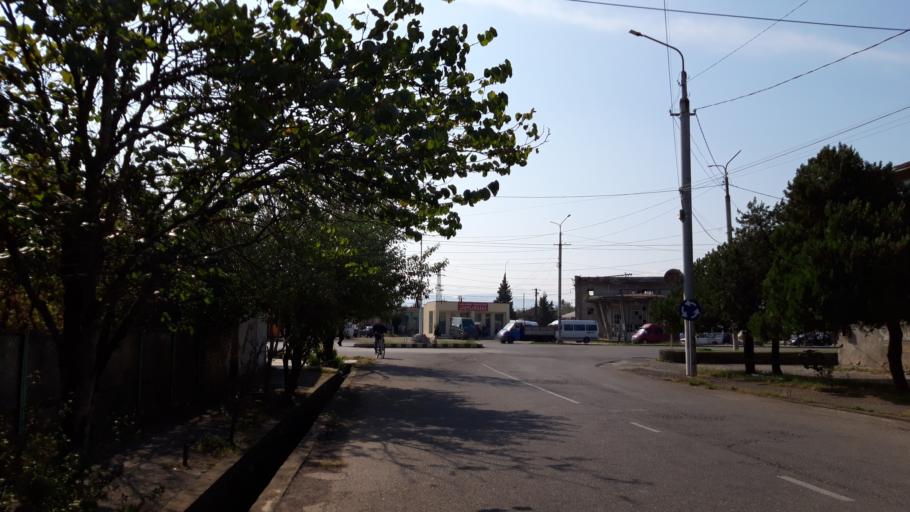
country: GE
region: Imereti
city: Samtredia
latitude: 42.1607
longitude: 42.3367
